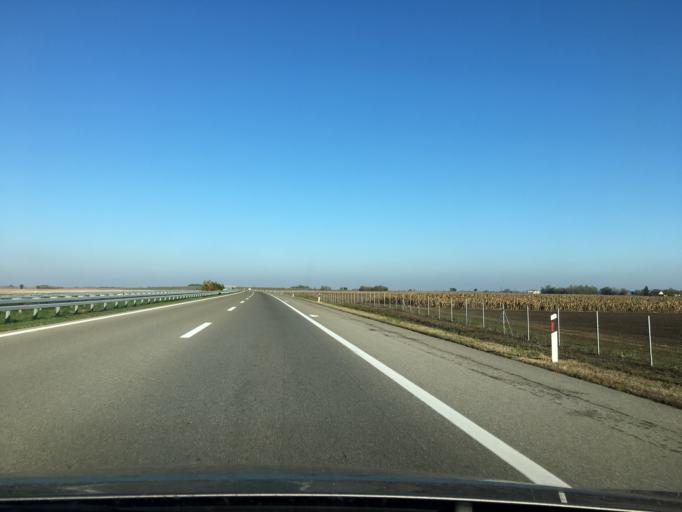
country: RS
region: Autonomna Pokrajina Vojvodina
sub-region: Severnobacki Okrug
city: Mali Igos
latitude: 45.7759
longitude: 19.6999
